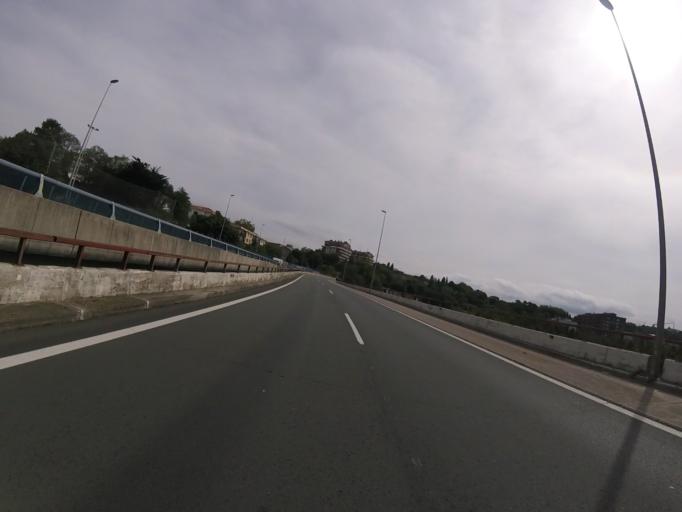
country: ES
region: Basque Country
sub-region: Provincia de Guipuzcoa
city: San Sebastian
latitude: 43.3089
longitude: -1.9696
